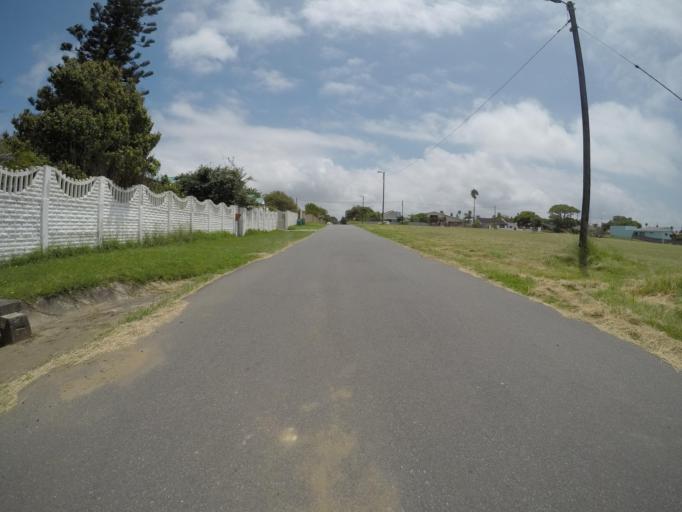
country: ZA
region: Eastern Cape
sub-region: Buffalo City Metropolitan Municipality
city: East London
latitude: -32.9468
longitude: 28.0150
